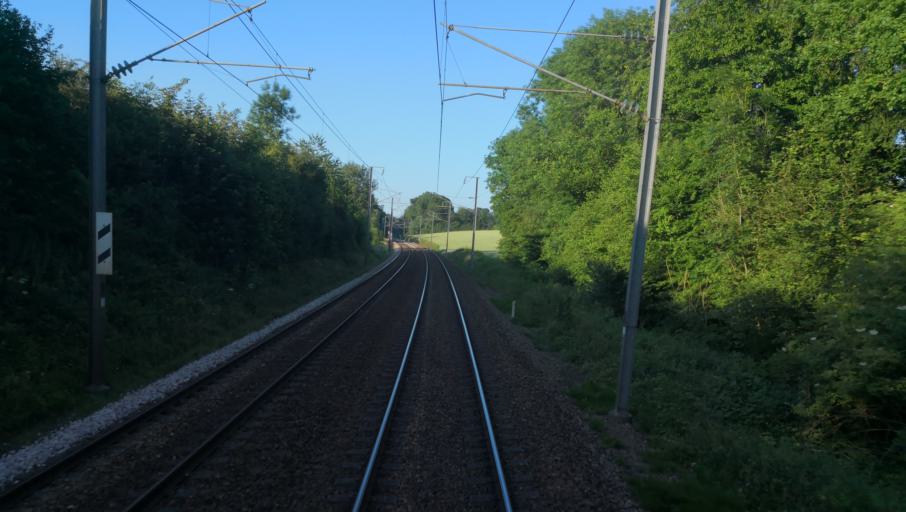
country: FR
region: Haute-Normandie
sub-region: Departement de l'Eure
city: Broglie
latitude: 49.0847
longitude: 0.5167
